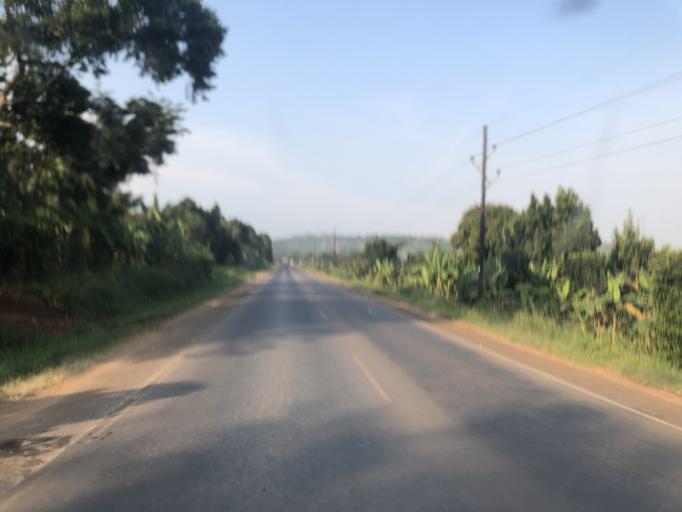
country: UG
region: Central Region
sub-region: Mpigi District
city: Mpigi
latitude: 0.1333
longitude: 32.2109
